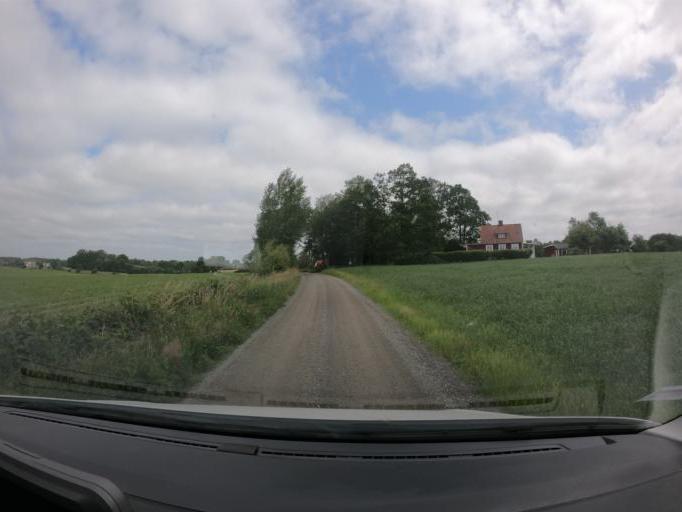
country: SE
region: Skane
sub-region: Hassleholms Kommun
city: Sosdala
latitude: 56.0632
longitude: 13.6600
